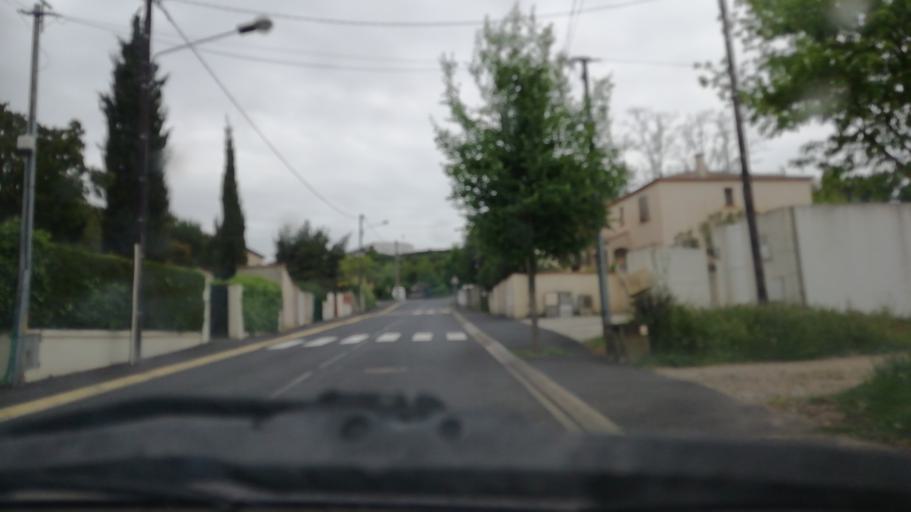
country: FR
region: Languedoc-Roussillon
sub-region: Departement de l'Herault
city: Boujan-sur-Libron
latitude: 43.3693
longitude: 3.2526
